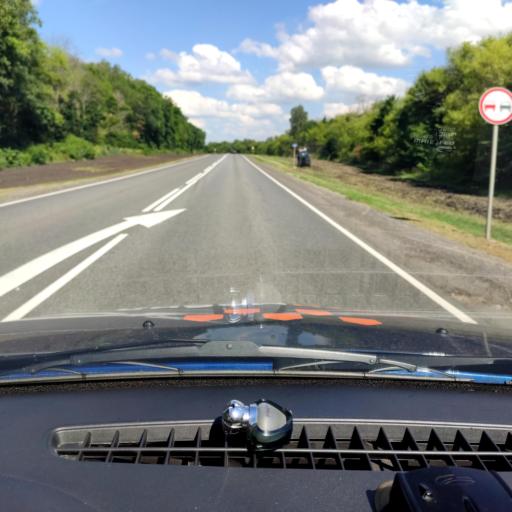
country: RU
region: Orjol
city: Livny
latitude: 52.4294
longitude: 37.8423
